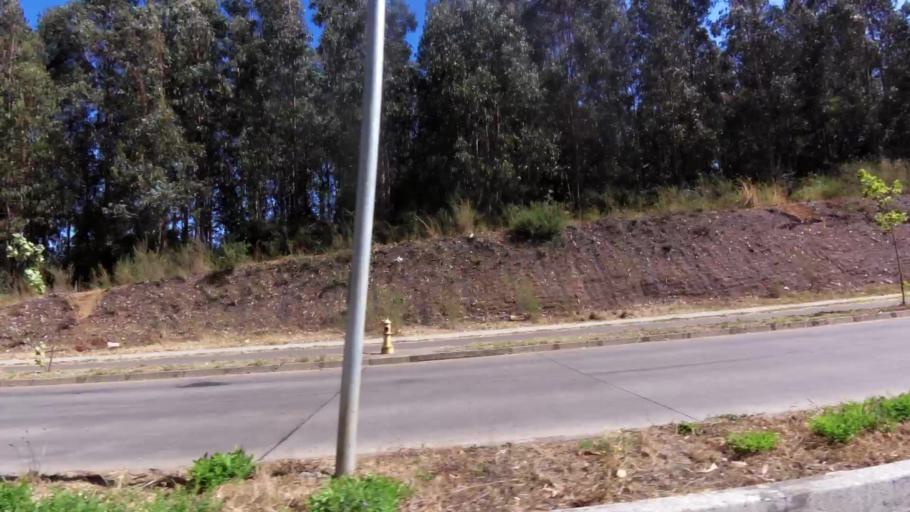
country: CL
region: Biobio
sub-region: Provincia de Concepcion
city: Concepcion
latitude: -36.7872
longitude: -73.0361
